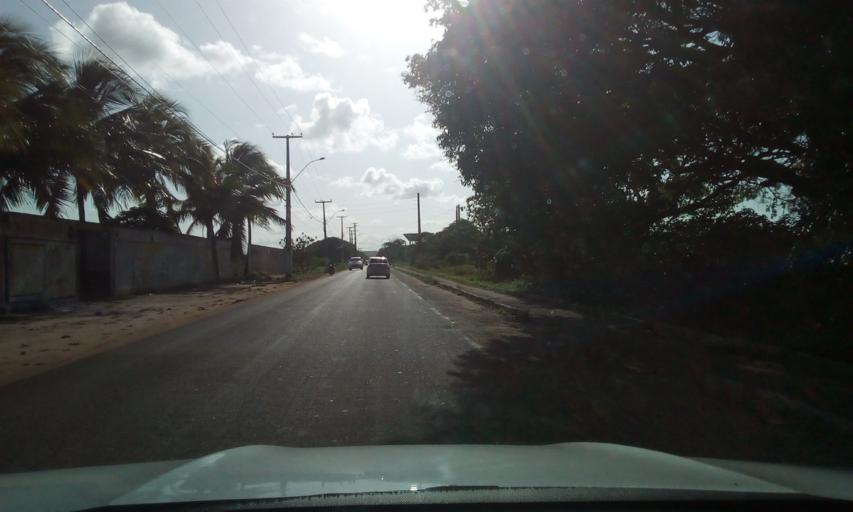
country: BR
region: Paraiba
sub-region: Cabedelo
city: Cabedelo
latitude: -7.0408
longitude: -34.8492
